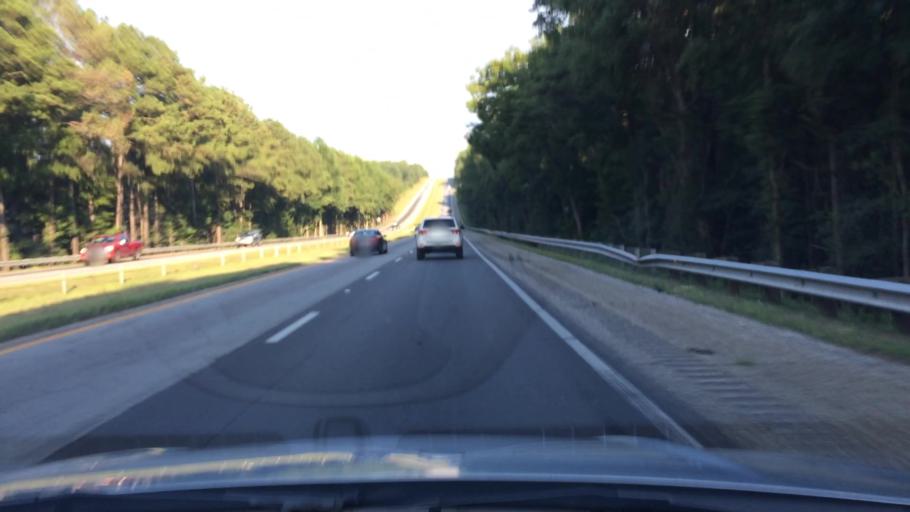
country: US
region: South Carolina
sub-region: Newberry County
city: Prosperity
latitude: 34.2323
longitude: -81.4423
